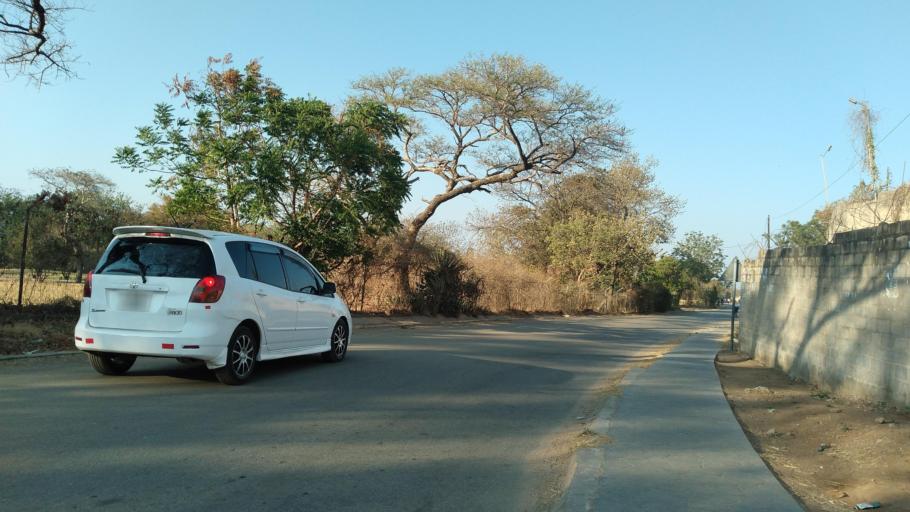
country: ZM
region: Lusaka
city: Lusaka
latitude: -15.5481
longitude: 28.2726
